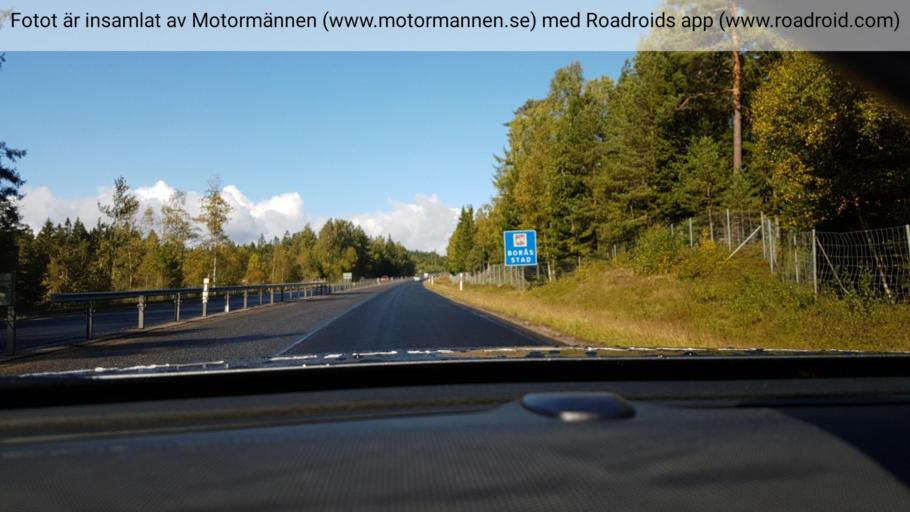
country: SE
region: Vaestra Goetaland
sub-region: Boras Kommun
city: Dalsjofors
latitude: 57.6272
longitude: 13.0935
